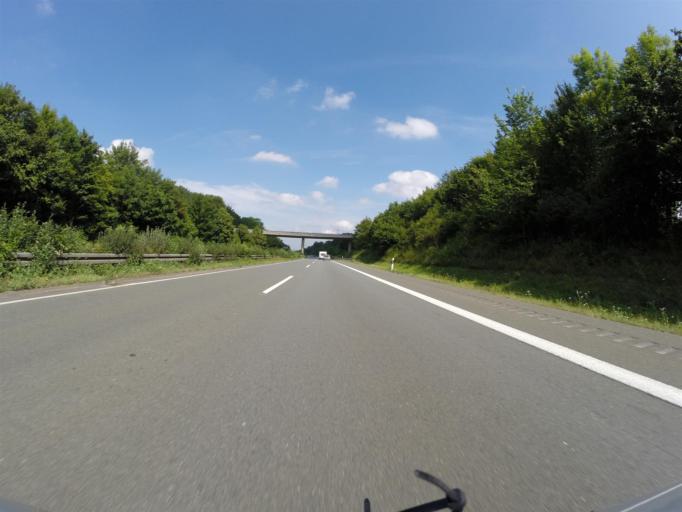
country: DE
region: North Rhine-Westphalia
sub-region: Regierungsbezirk Detmold
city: Paderborn
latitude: 51.6813
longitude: 8.7138
